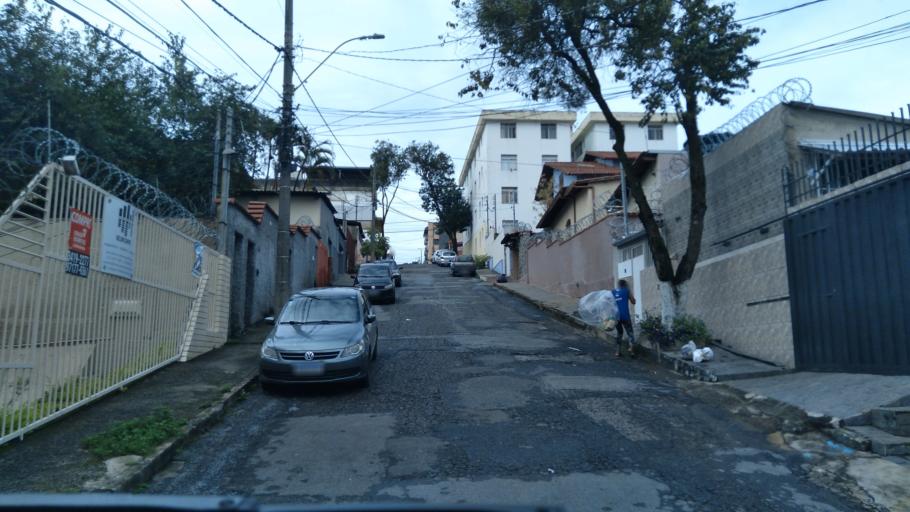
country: BR
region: Minas Gerais
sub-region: Contagem
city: Contagem
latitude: -19.9271
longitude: -43.9976
